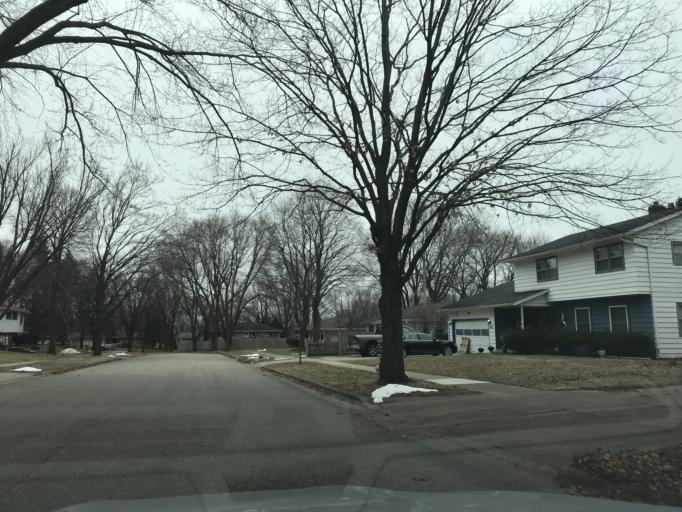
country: US
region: Wisconsin
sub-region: Dane County
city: Monona
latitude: 43.0909
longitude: -89.3010
